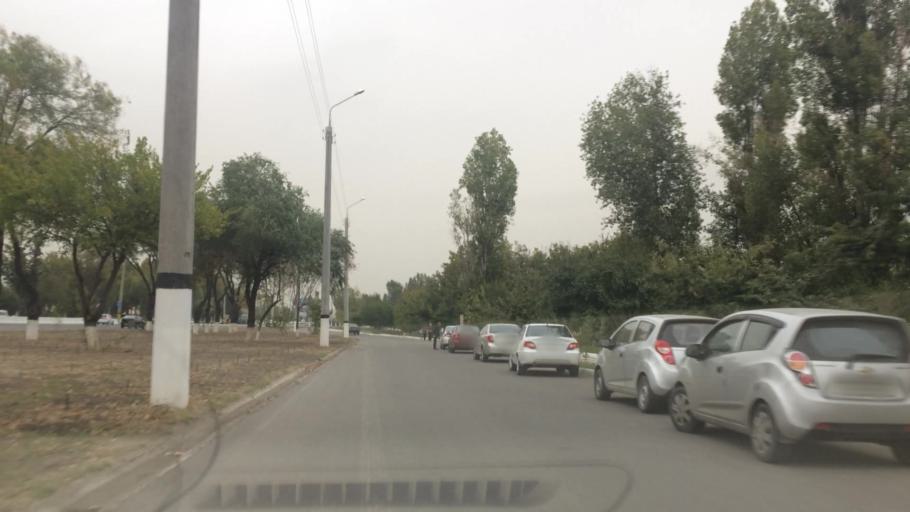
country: UZ
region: Toshkent
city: Salor
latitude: 41.3115
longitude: 69.3476
